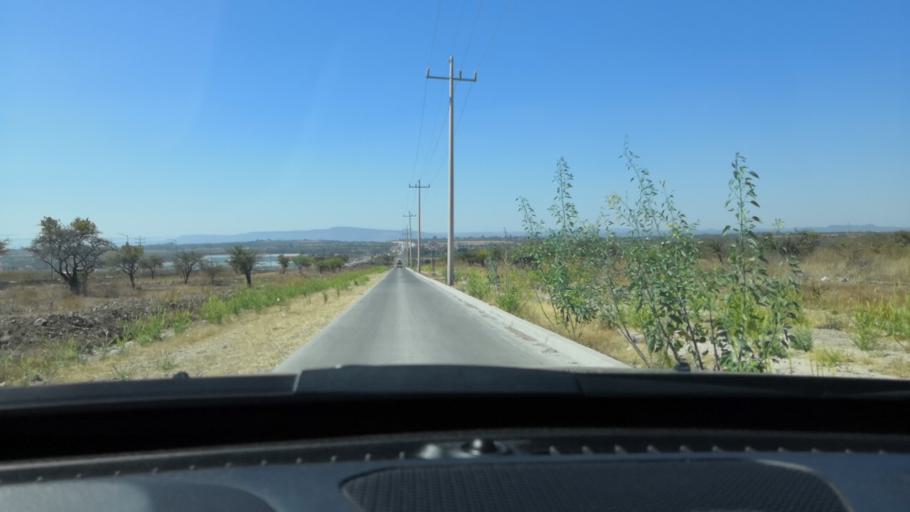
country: MX
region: Guanajuato
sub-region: Leon
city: Centro Familiar la Soledad
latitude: 21.1097
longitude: -101.7599
